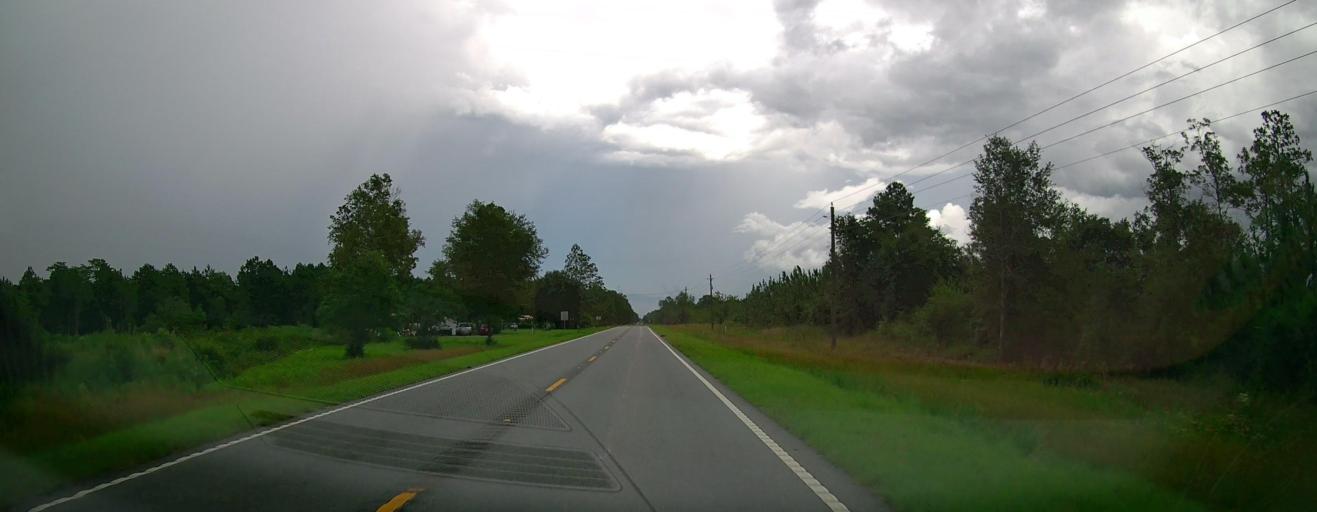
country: US
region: Georgia
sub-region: Pierce County
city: Blackshear
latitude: 31.3668
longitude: -82.0900
